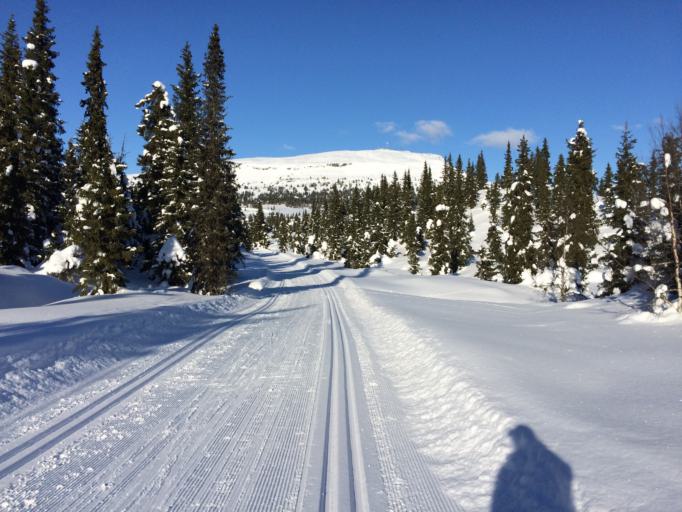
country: NO
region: Oppland
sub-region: Gausdal
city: Segalstad bru
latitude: 61.3349
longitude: 10.0599
